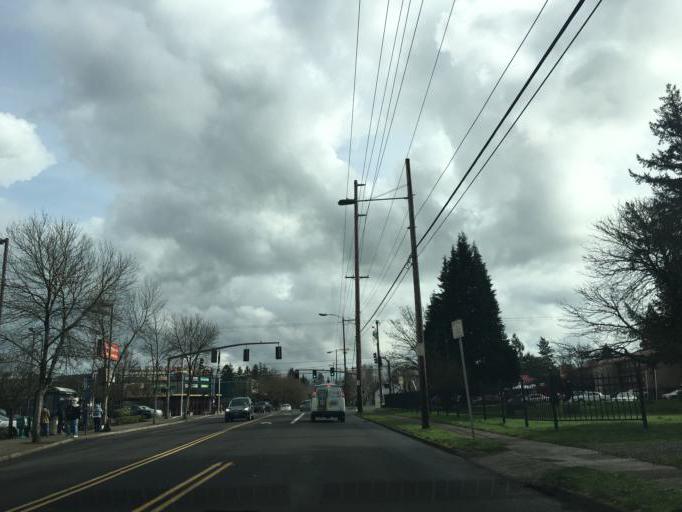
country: US
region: Oregon
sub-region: Multnomah County
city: Lents
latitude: 45.4902
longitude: -122.5799
